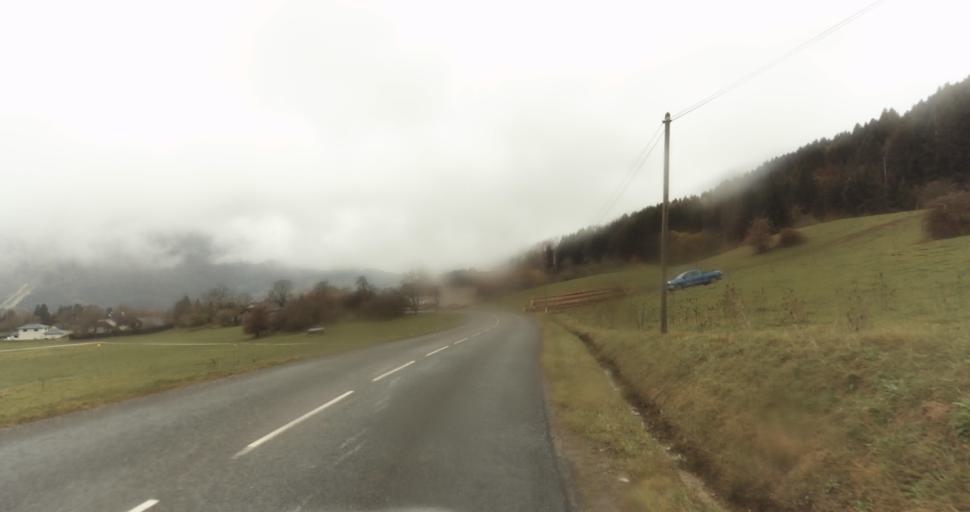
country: FR
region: Rhone-Alpes
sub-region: Departement de la Haute-Savoie
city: Thorens-Glieres
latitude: 46.0073
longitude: 6.2595
